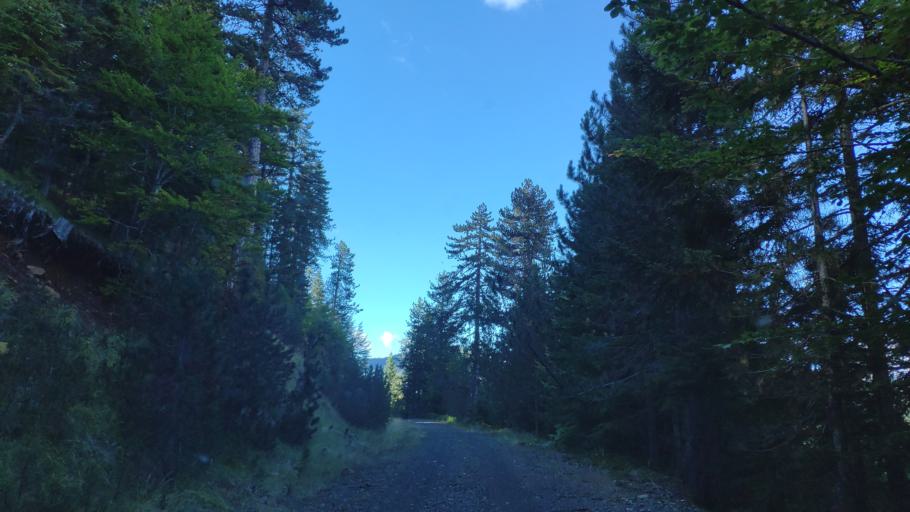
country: GR
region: Epirus
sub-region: Nomos Ioanninon
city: Metsovo
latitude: 39.8910
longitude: 21.2094
